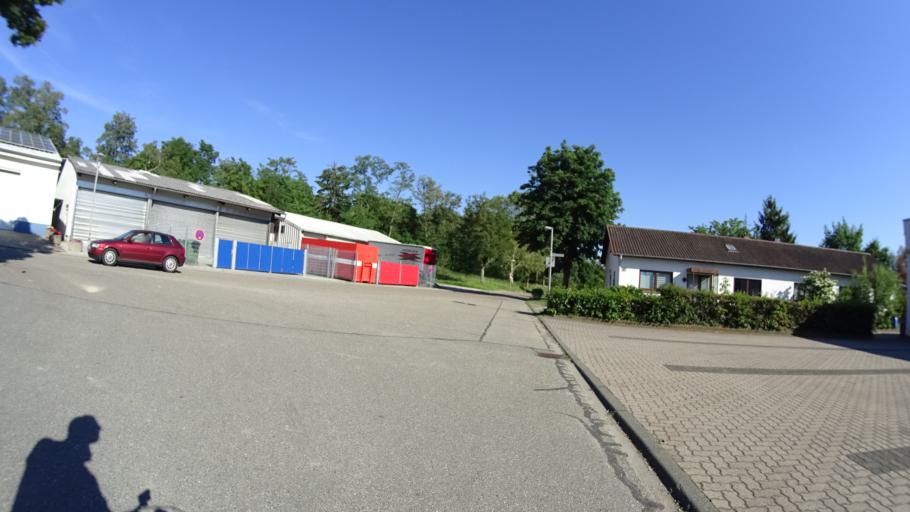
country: DE
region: Baden-Wuerttemberg
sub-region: Karlsruhe Region
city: Eggenstein-Leopoldshafen
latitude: 49.0967
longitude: 8.3942
